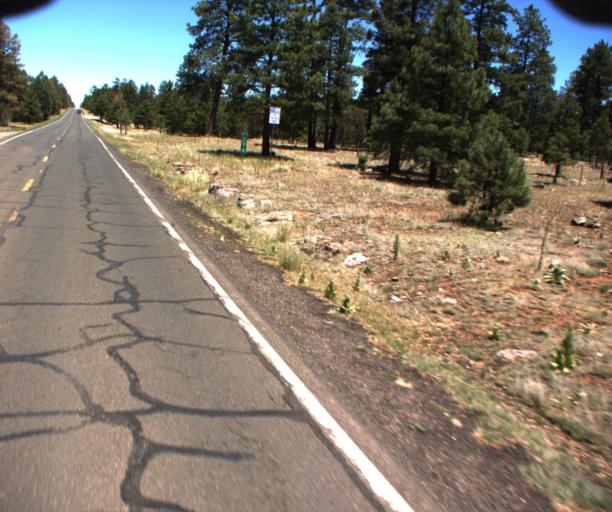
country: US
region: Arizona
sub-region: Gila County
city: Pine
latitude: 34.5748
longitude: -111.2676
